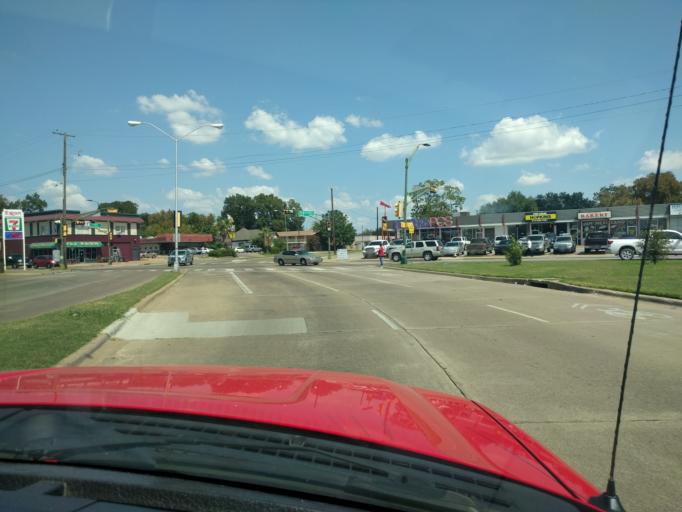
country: US
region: Texas
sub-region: Dallas County
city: Dallas
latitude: 32.7911
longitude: -96.7676
